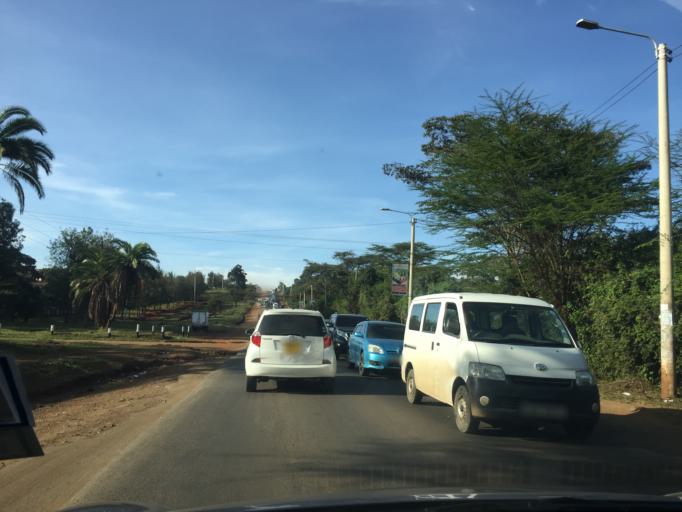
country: KE
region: Nairobi Area
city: Nairobi
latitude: -1.3803
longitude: 36.7703
